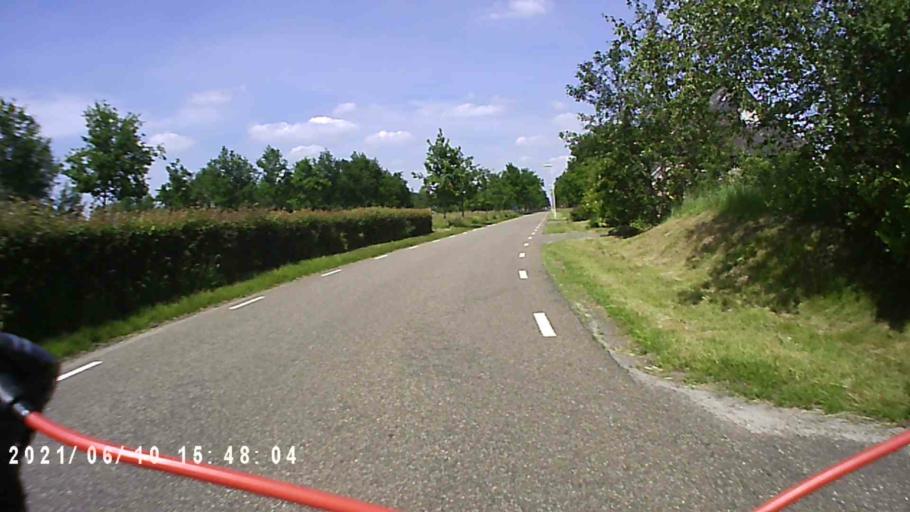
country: NL
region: Friesland
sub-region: Gemeente Smallingerland
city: Rottevalle
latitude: 53.1633
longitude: 6.1182
